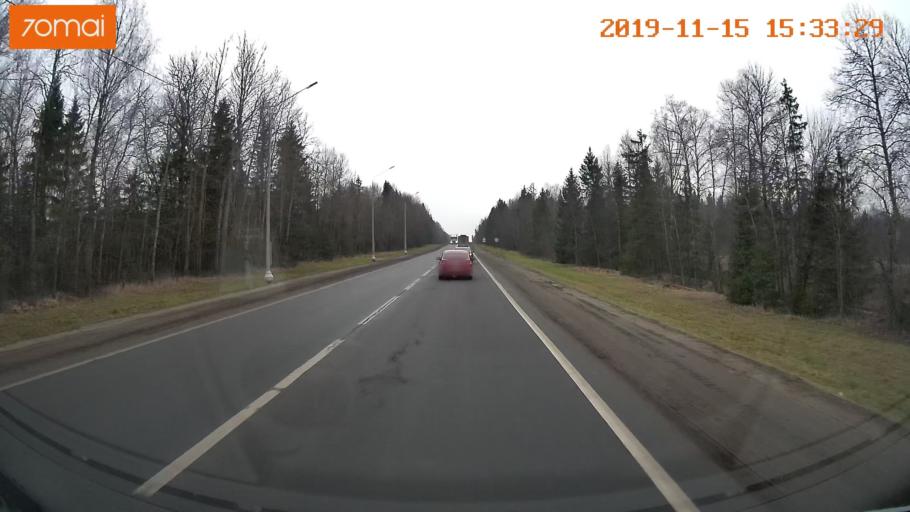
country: RU
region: Jaroslavl
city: Danilov
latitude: 58.0799
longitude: 40.0924
